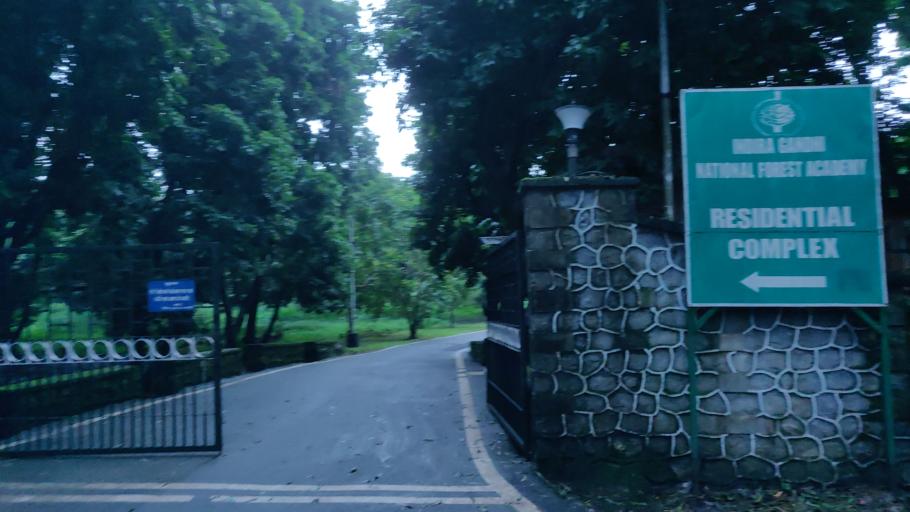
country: IN
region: Uttarakhand
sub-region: Dehradun
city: Dehradun
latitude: 30.3325
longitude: 77.9940
